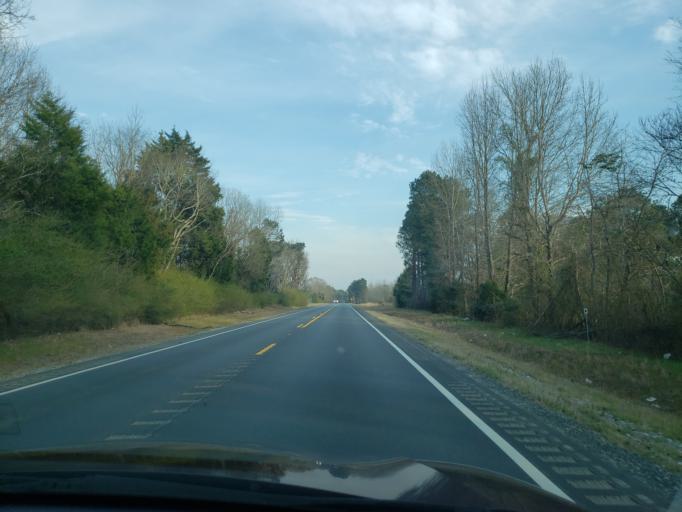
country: US
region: Alabama
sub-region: Hale County
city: Moundville
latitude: 32.8938
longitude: -87.6179
